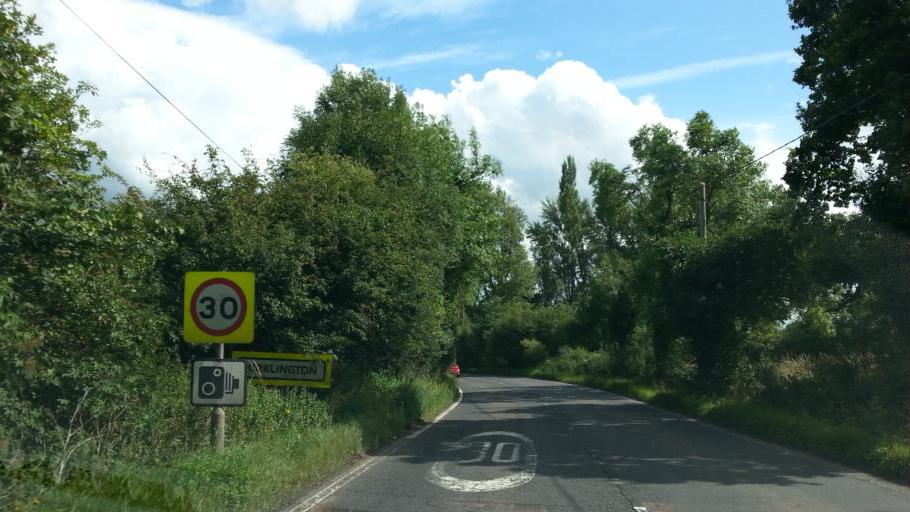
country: GB
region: England
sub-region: Nottinghamshire
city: Farnsfield
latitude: 53.1135
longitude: -0.9909
